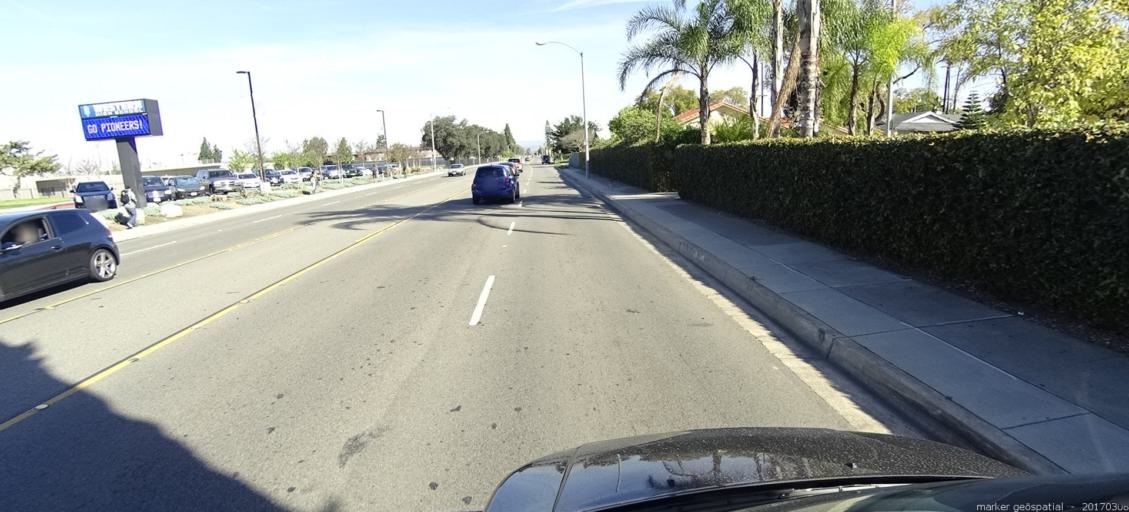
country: US
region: California
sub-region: Orange County
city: Stanton
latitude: 33.8256
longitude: -118.0021
